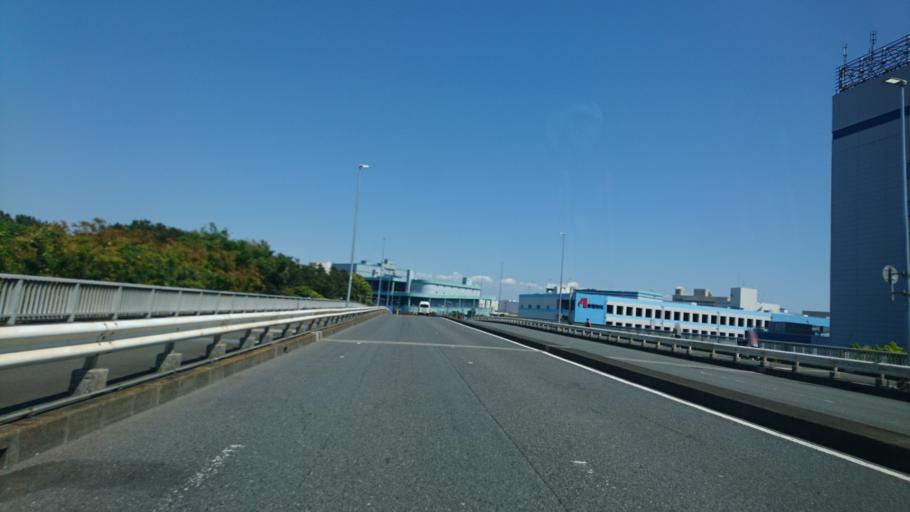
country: JP
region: Kanagawa
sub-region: Kawasaki-shi
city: Kawasaki
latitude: 35.5951
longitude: 139.7607
